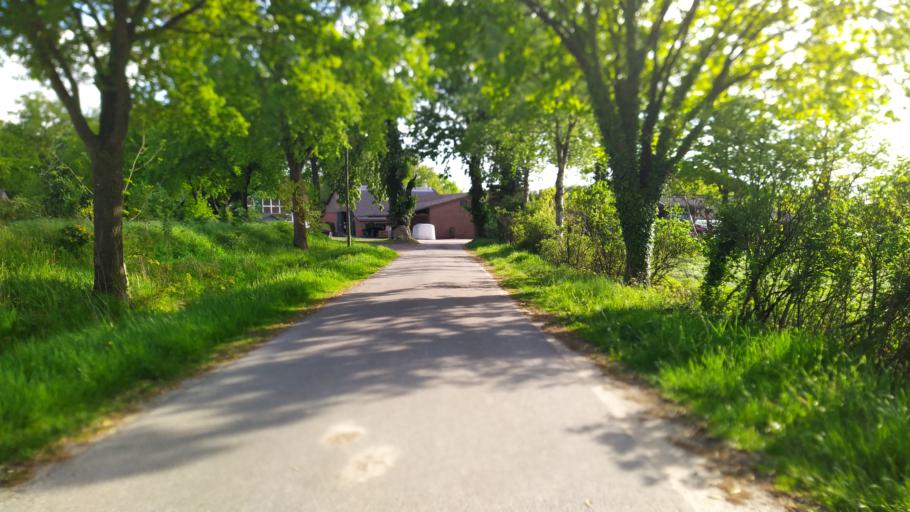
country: DE
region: Lower Saxony
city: Brest
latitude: 53.4019
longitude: 9.3616
